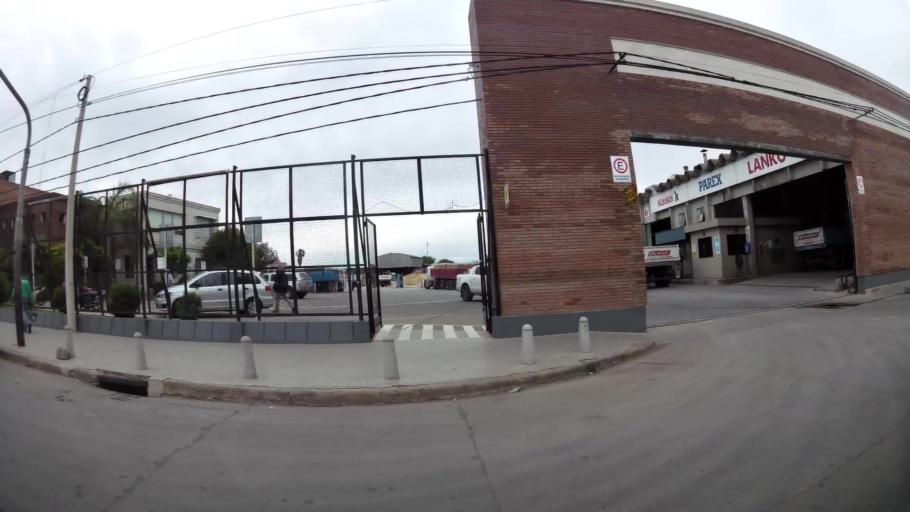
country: AR
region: Santa Fe
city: Gobernador Galvez
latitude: -32.9912
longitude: -60.6640
